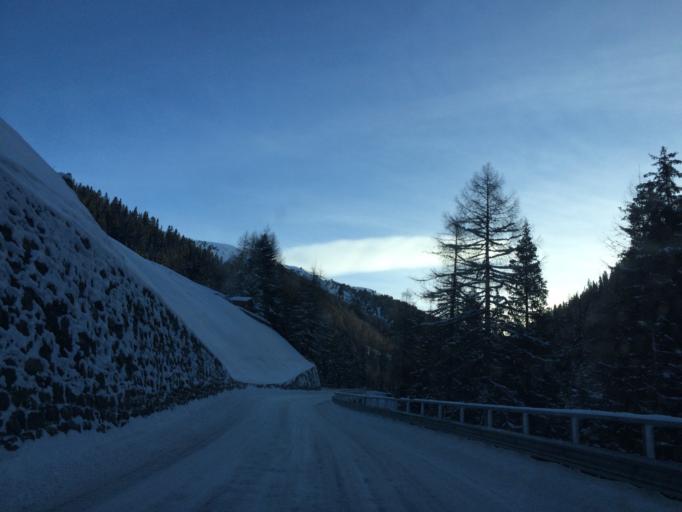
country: CH
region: Grisons
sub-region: Praettigau/Davos District
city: Davos
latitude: 46.8069
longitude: 9.8831
